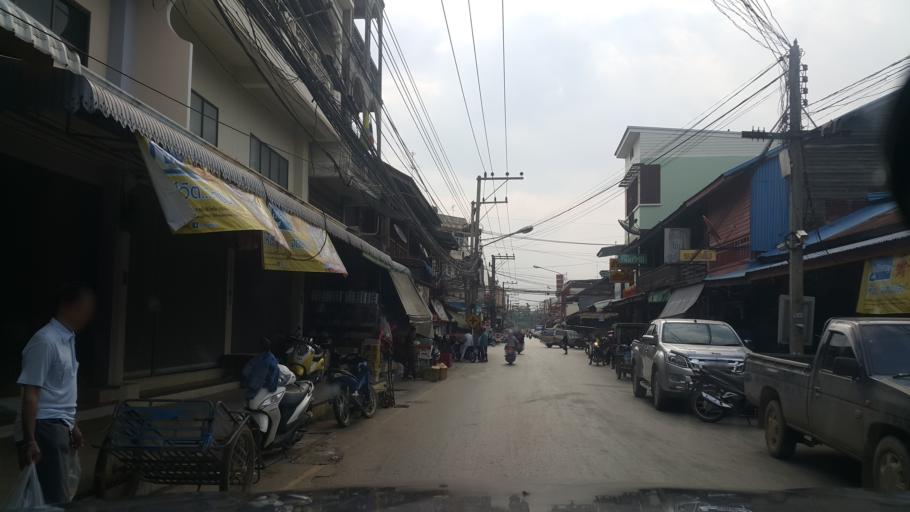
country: TH
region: Sukhothai
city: Si Samrong
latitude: 17.1683
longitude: 99.8617
